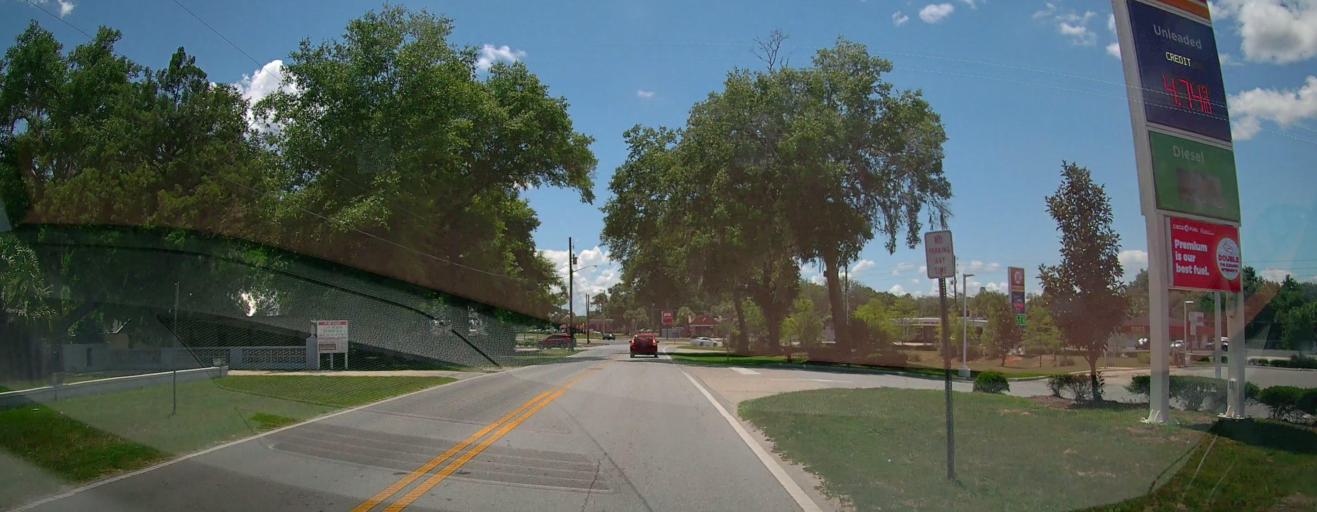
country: US
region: Florida
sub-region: Marion County
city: Ocala
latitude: 29.2120
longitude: -82.0623
